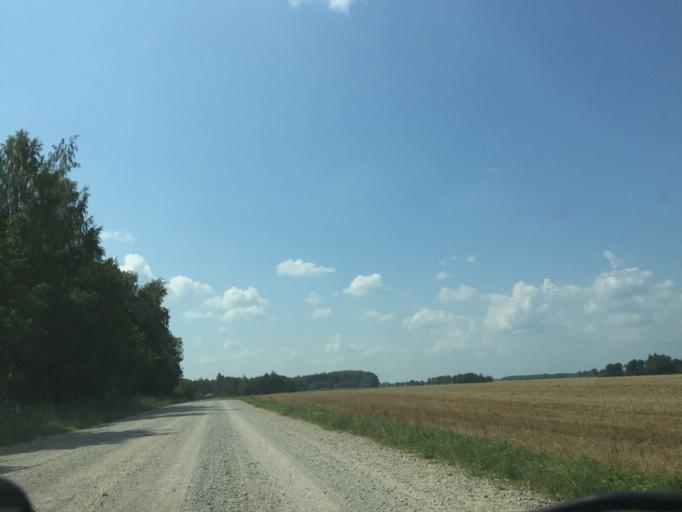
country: LT
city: Zagare
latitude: 56.3780
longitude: 23.2842
